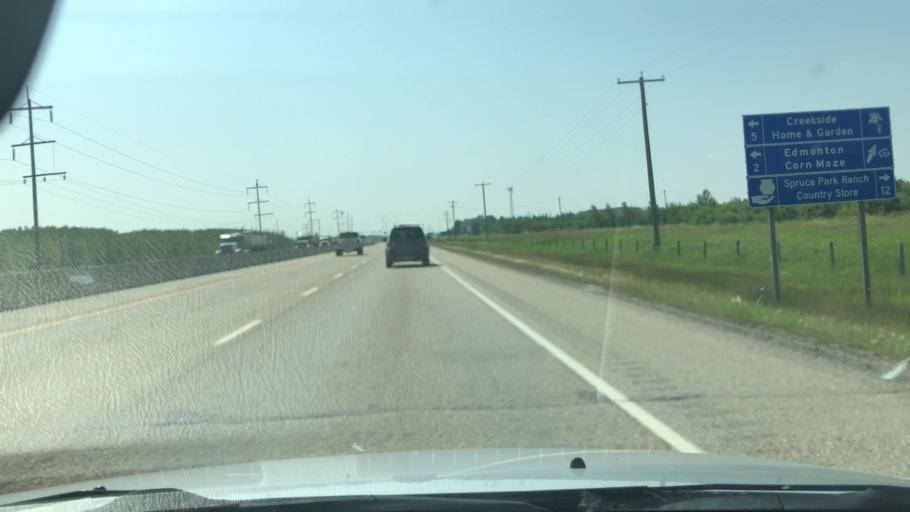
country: CA
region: Alberta
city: Devon
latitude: 53.4589
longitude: -113.7626
